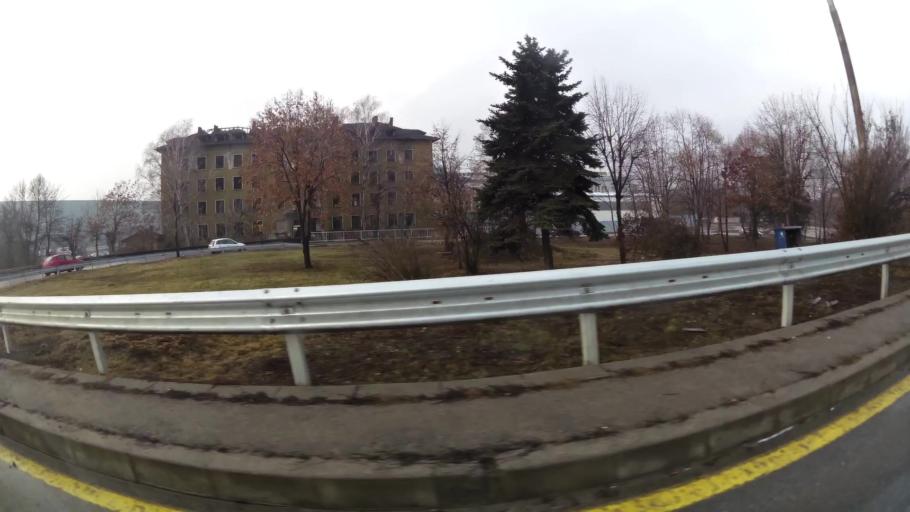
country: BG
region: Sofia-Capital
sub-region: Stolichna Obshtina
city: Sofia
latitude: 42.7196
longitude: 23.3133
